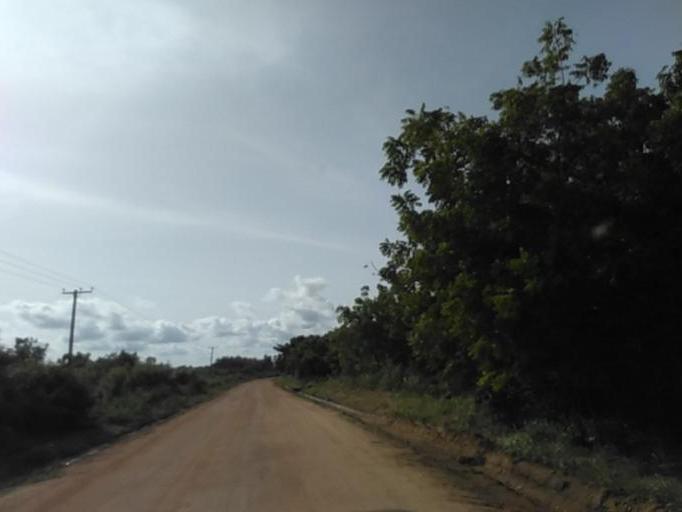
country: GH
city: Akropong
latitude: 6.0568
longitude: 0.2923
